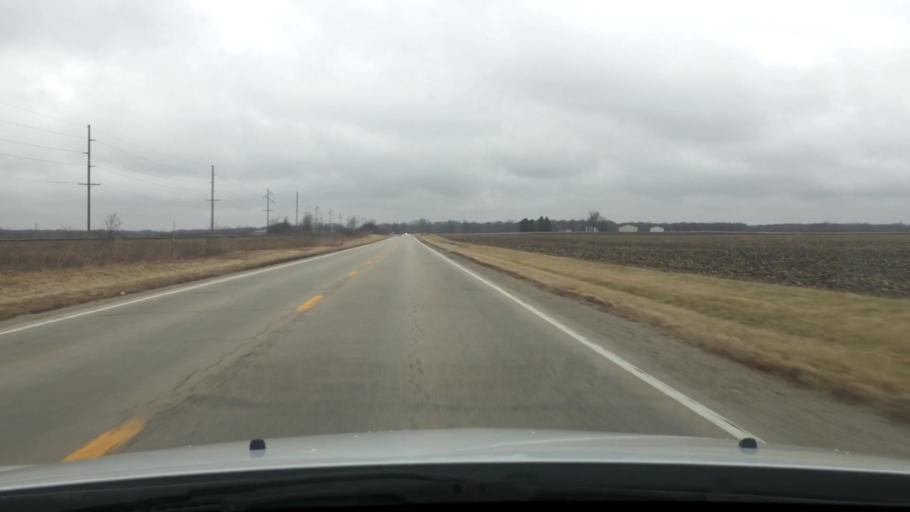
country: US
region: Illinois
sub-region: Iroquois County
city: Sheldon
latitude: 40.8008
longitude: -87.5728
